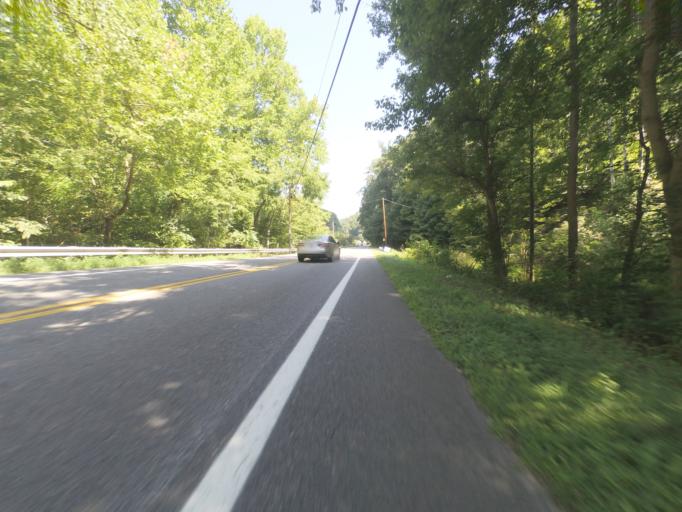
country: US
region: West Virginia
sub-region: Cabell County
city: Huntington
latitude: 38.3725
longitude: -82.4551
